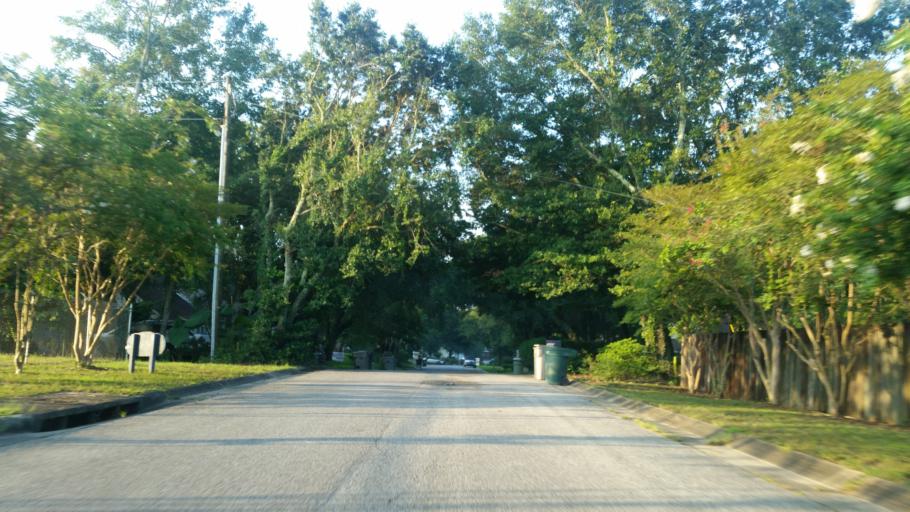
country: US
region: Florida
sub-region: Escambia County
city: Ferry Pass
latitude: 30.5001
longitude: -87.2336
